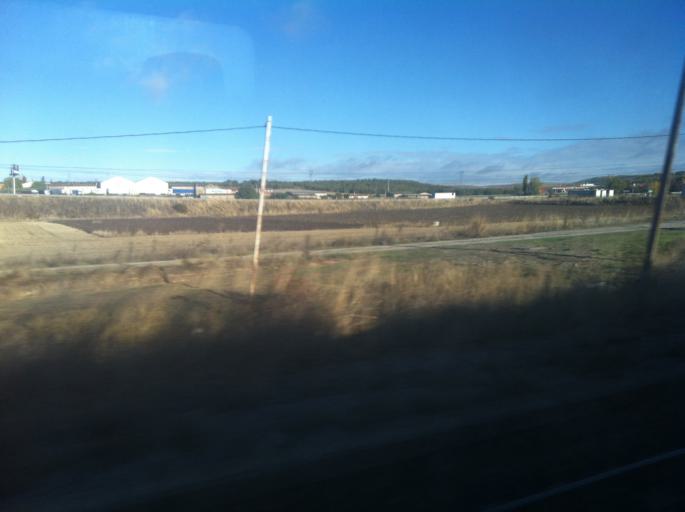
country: ES
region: Castille and Leon
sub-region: Provincia de Burgos
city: Estepar
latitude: 42.2720
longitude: -3.8948
